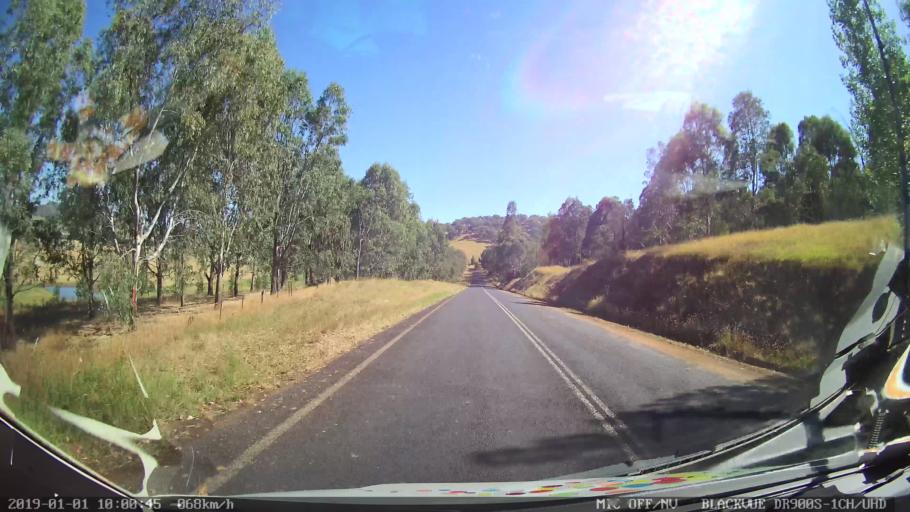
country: AU
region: New South Wales
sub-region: Snowy River
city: Jindabyne
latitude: -36.1988
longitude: 148.1025
